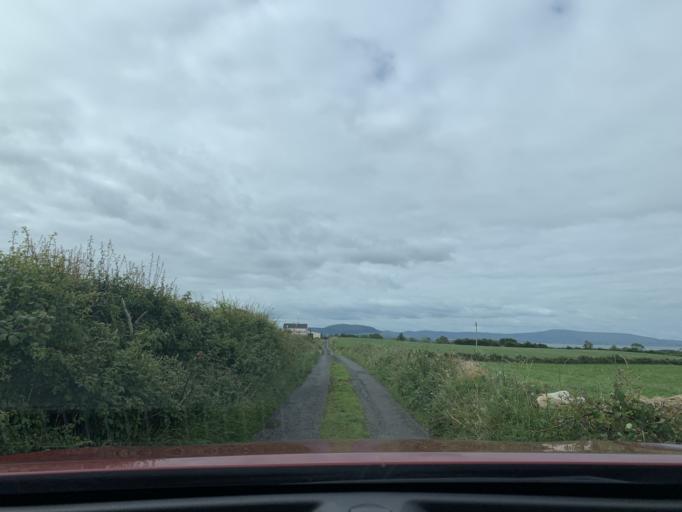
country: IE
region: Connaught
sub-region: Sligo
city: Sligo
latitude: 54.3637
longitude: -8.5219
